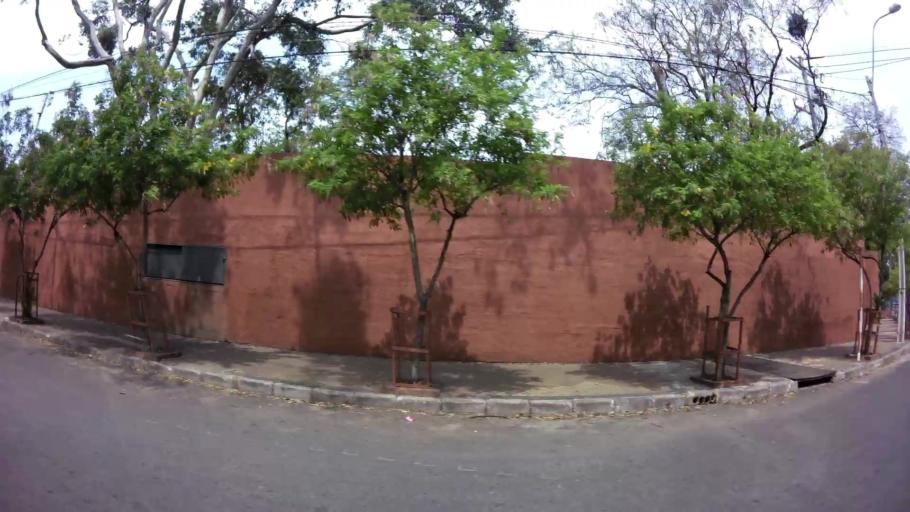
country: PY
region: Asuncion
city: Asuncion
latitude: -25.2838
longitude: -57.5805
